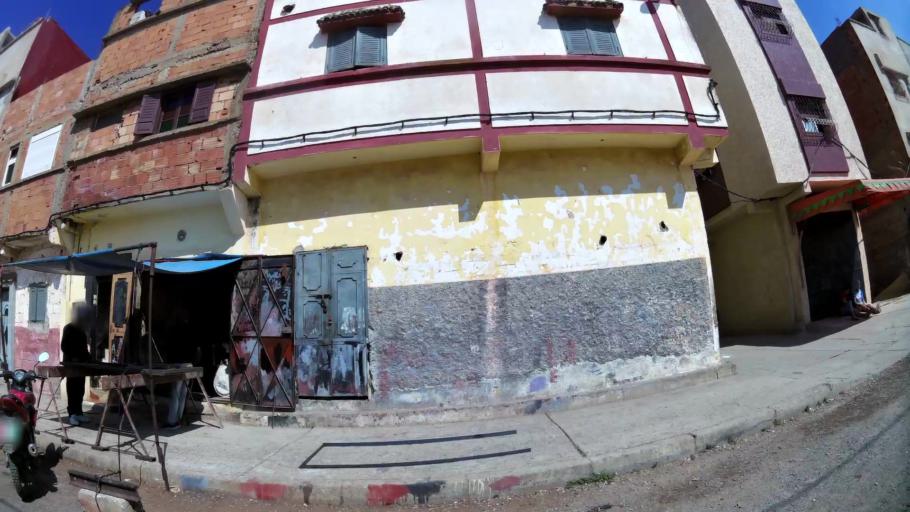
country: MA
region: Rabat-Sale-Zemmour-Zaer
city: Sale
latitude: 34.0710
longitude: -6.7708
